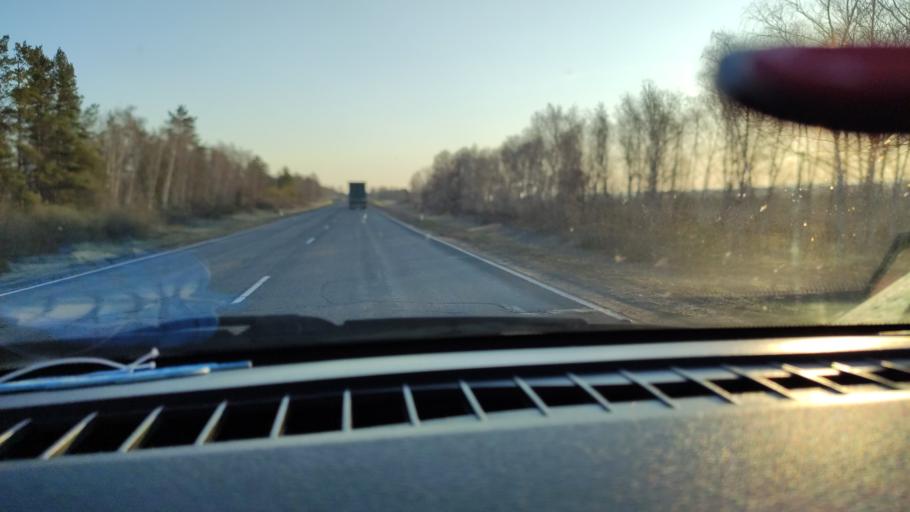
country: RU
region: Saratov
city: Sennoy
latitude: 52.1062
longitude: 46.8222
